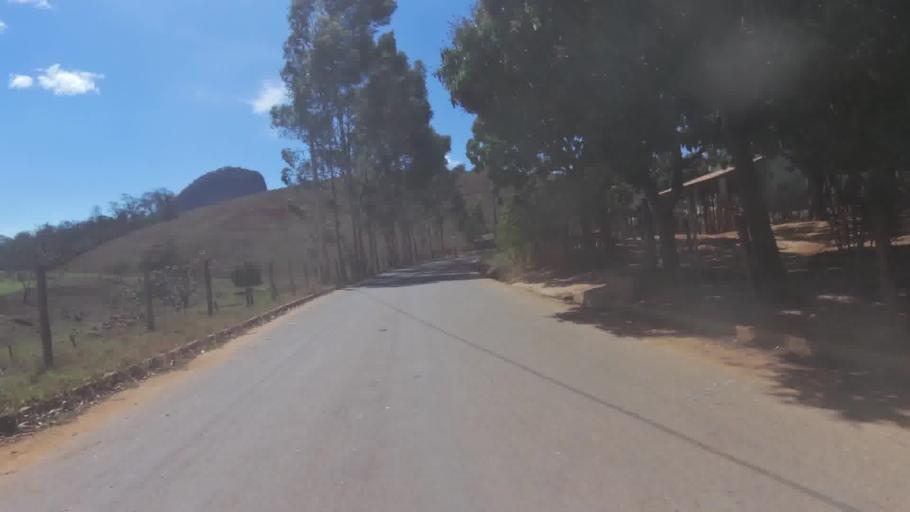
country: BR
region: Espirito Santo
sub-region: Cachoeiro De Itapemirim
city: Cachoeiro de Itapemirim
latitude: -20.9228
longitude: -41.2102
